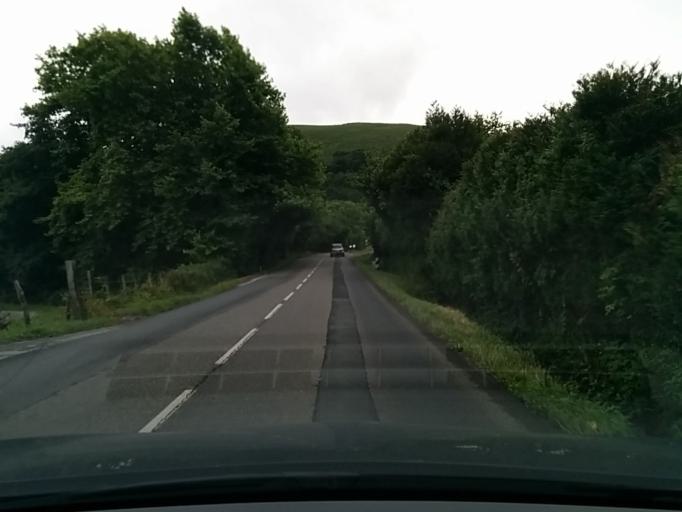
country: FR
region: Aquitaine
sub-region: Departement des Pyrenees-Atlantiques
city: Saint-Pee-sur-Nivelle
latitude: 43.3313
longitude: -1.5455
